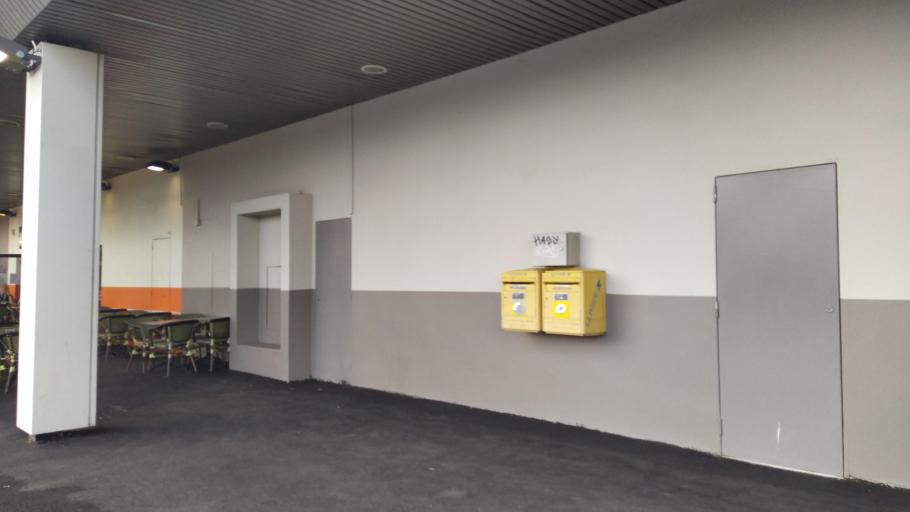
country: FR
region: Pays de la Loire
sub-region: Departement de la Loire-Atlantique
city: Sainte-Luce-sur-Loire
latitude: 47.2574
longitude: -1.5127
